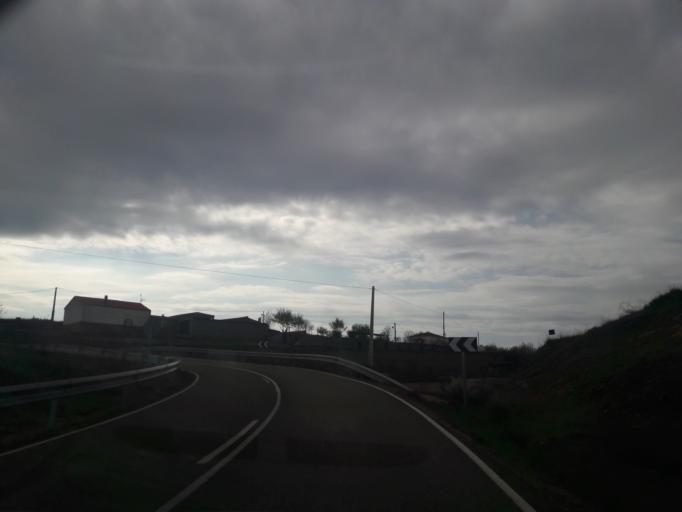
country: ES
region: Castille and Leon
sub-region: Provincia de Salamanca
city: Pastores
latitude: 40.5135
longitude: -6.5131
